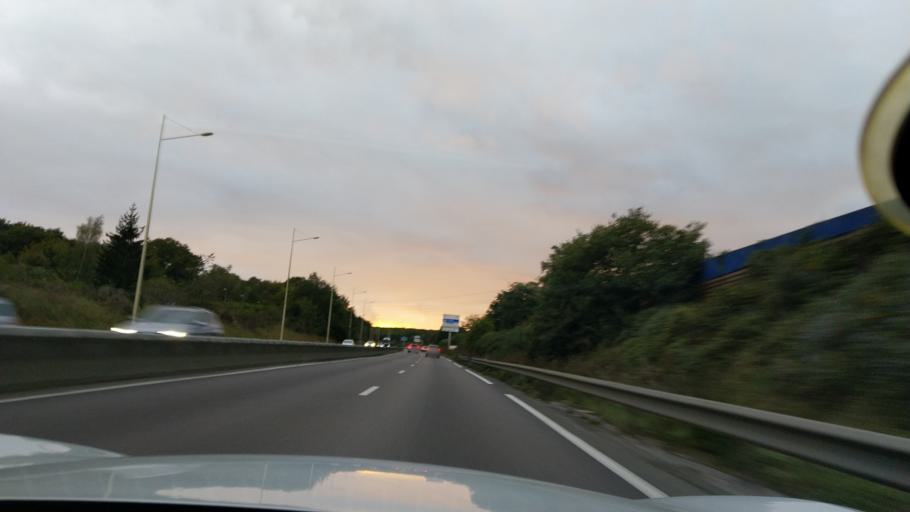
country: FR
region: Haute-Normandie
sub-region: Departement de la Seine-Maritime
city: Saint-Etienne-du-Rouvray
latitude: 49.3677
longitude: 1.1016
